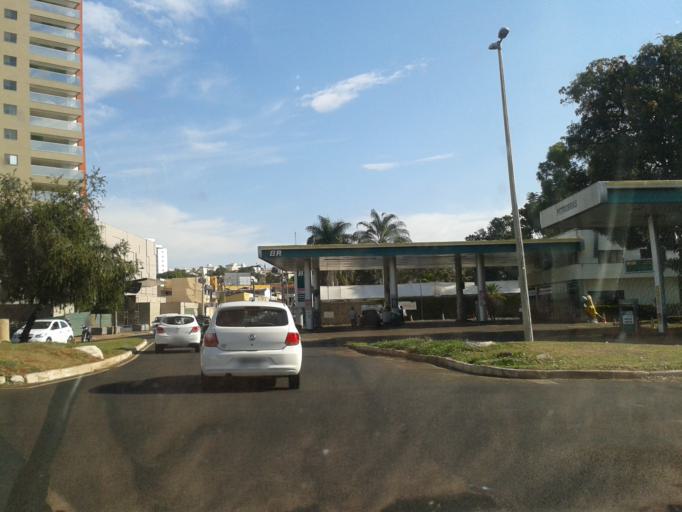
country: BR
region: Minas Gerais
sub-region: Uberlandia
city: Uberlandia
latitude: -18.9296
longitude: -48.2937
